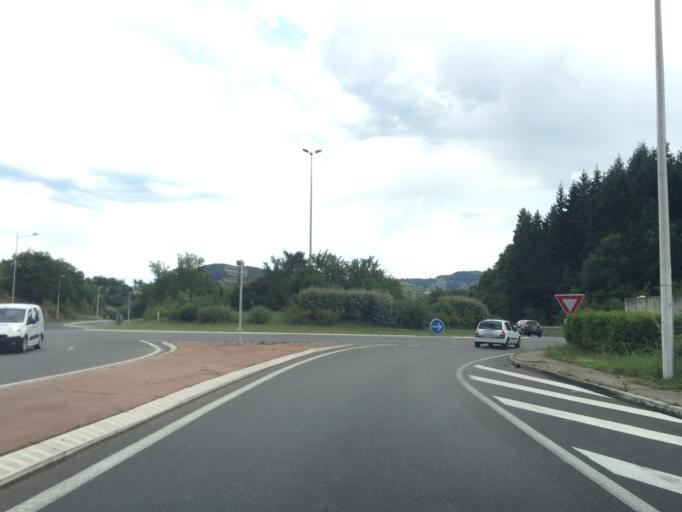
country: FR
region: Rhone-Alpes
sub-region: Departement du Rhone
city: Pontcharra-sur-Turdine
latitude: 45.8796
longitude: 4.4745
